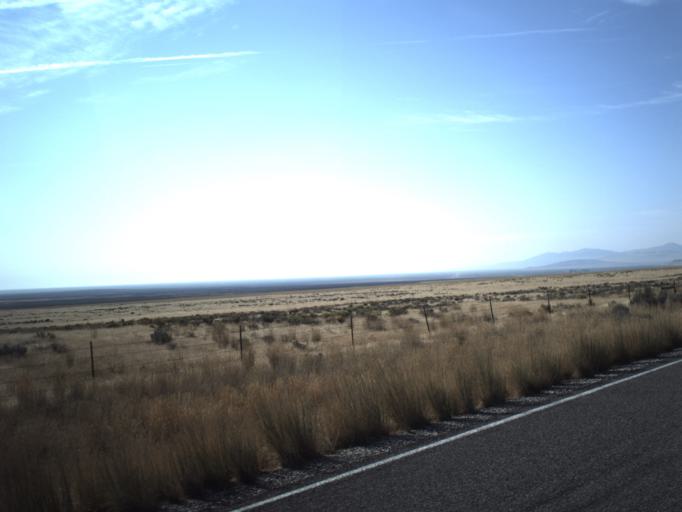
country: US
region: Idaho
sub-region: Oneida County
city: Malad City
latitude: 41.8700
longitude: -113.1235
